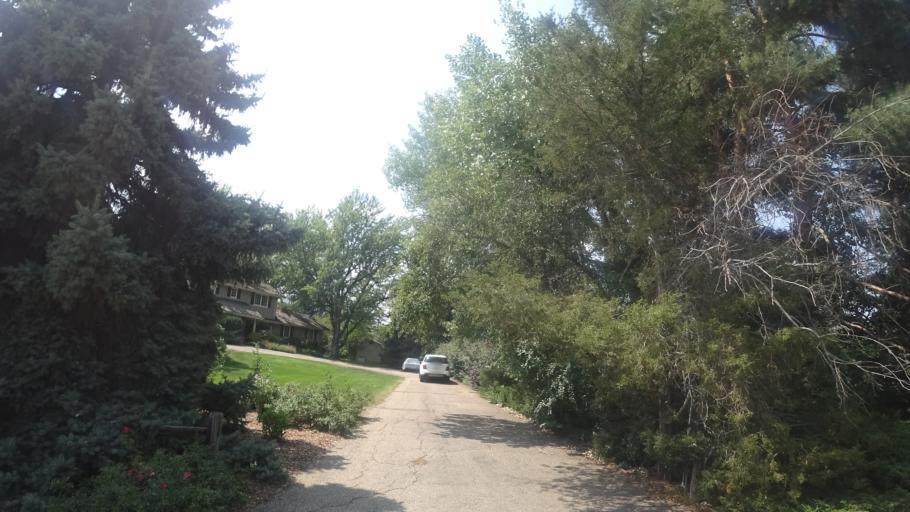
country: US
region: Colorado
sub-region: Arapahoe County
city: Greenwood Village
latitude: 39.6224
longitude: -104.9693
